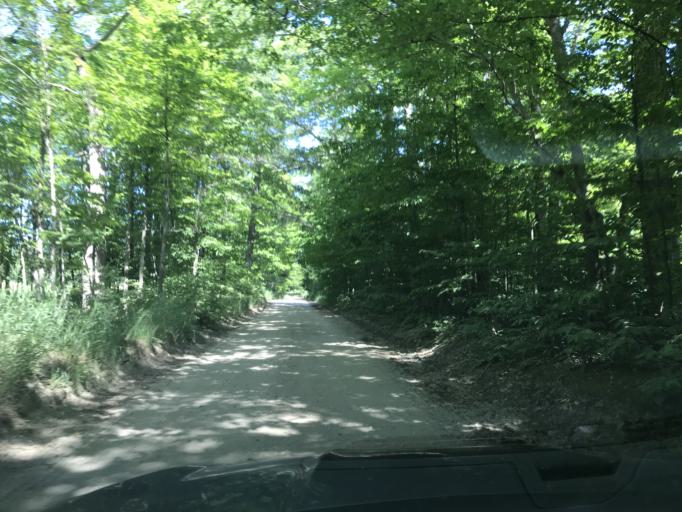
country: US
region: Michigan
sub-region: Cheboygan County
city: Indian River
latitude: 45.6036
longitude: -84.6740
